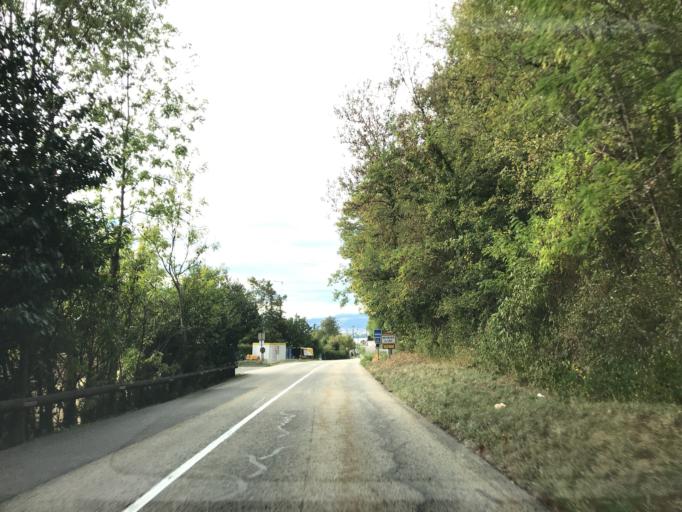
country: FR
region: Rhone-Alpes
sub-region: Departement de la Haute-Savoie
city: Menthon-Saint-Bernard
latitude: 45.8702
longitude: 6.1884
